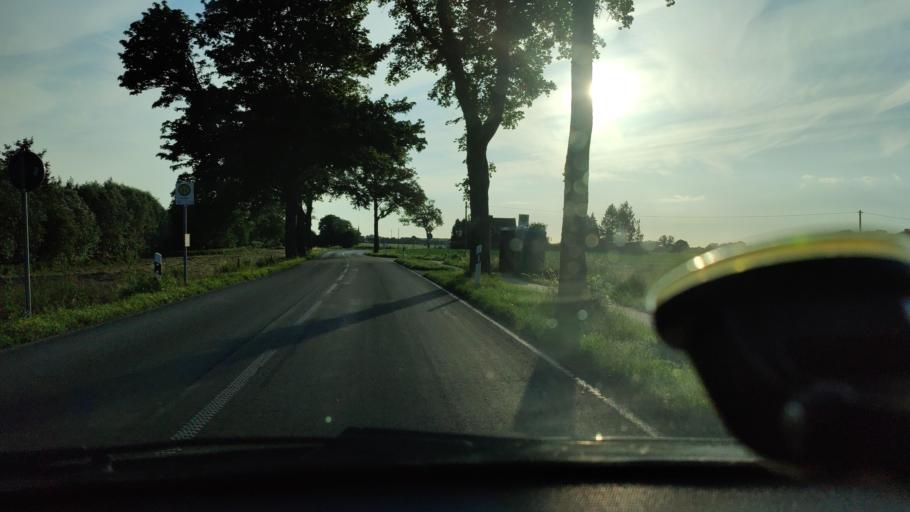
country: DE
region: North Rhine-Westphalia
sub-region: Regierungsbezirk Dusseldorf
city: Rheurdt
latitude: 51.5100
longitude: 6.4865
